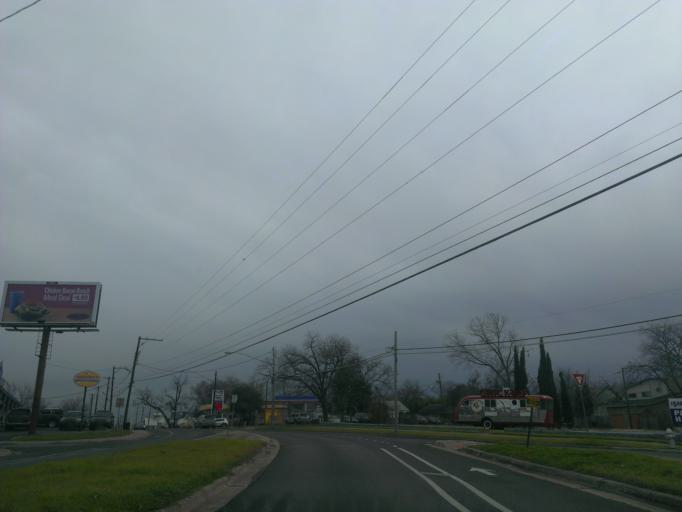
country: US
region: Texas
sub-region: Travis County
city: Austin
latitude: 30.2841
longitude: -97.7214
